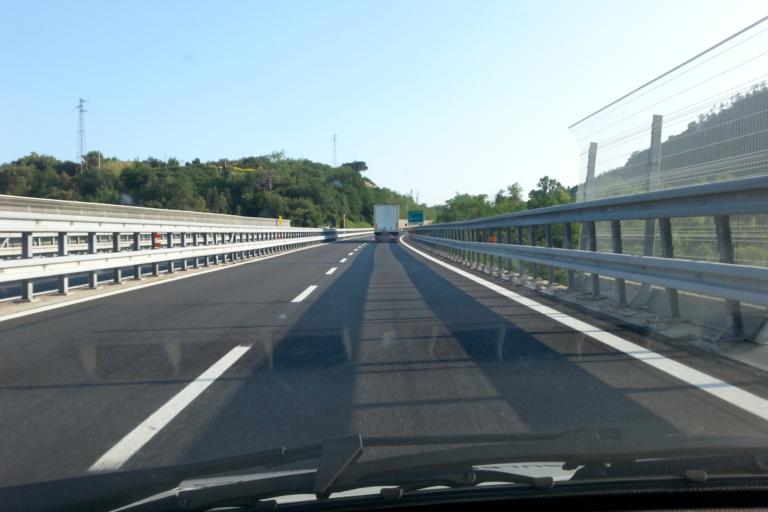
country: IT
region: Liguria
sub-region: Provincia di Savona
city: Pietra Ligure
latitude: 44.1612
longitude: 8.2740
